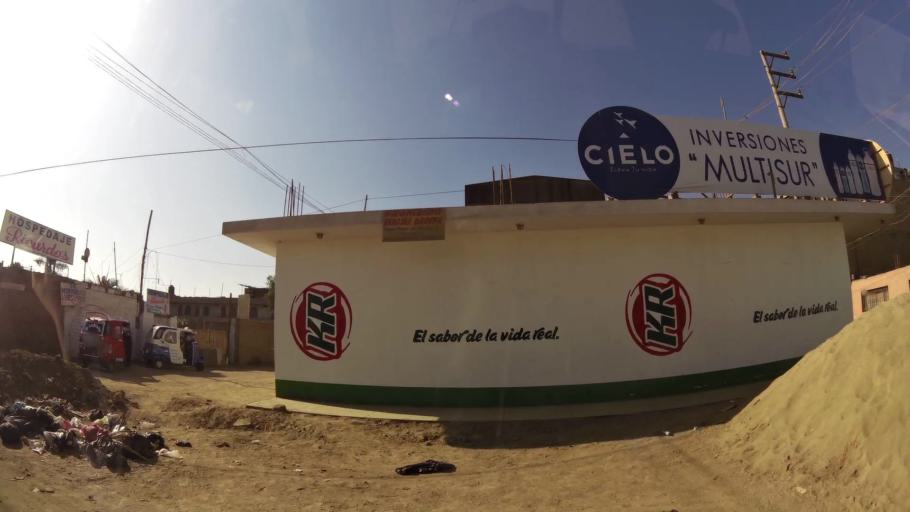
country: PE
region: Ica
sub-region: Provincia de Chincha
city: Chincha Alta
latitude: -13.4131
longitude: -76.1390
